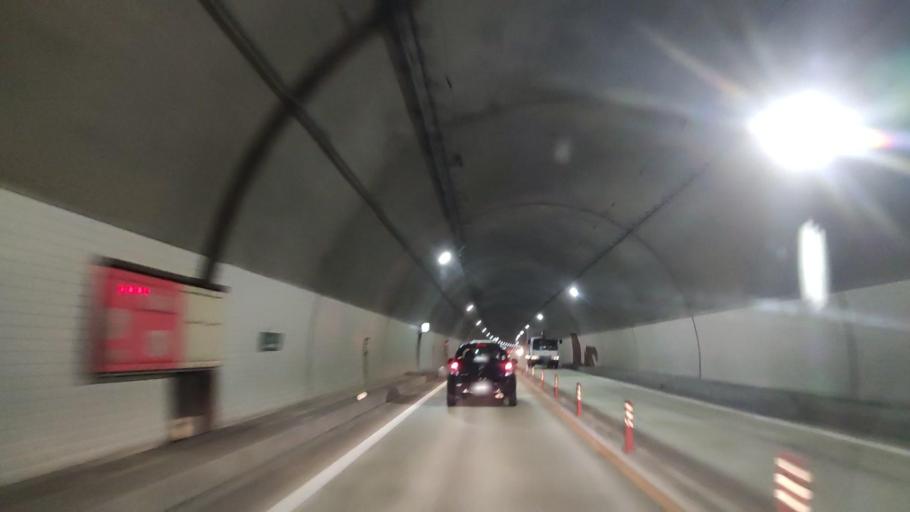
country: JP
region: Akita
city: Odate
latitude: 40.2253
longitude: 140.4698
